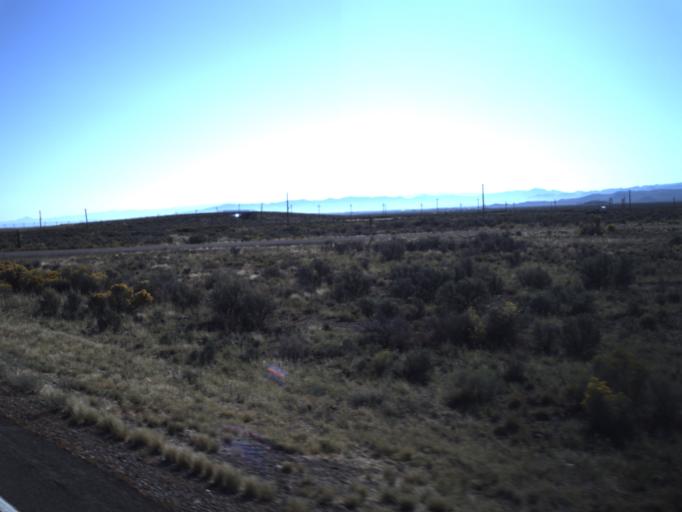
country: US
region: Utah
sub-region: Washington County
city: Enterprise
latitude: 37.8022
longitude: -113.9265
